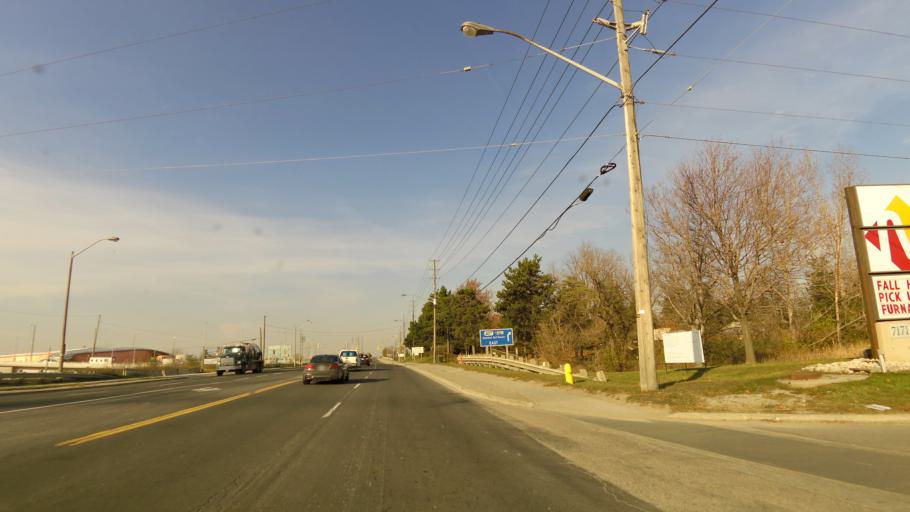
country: CA
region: Ontario
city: Concord
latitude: 43.7808
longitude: -79.5211
